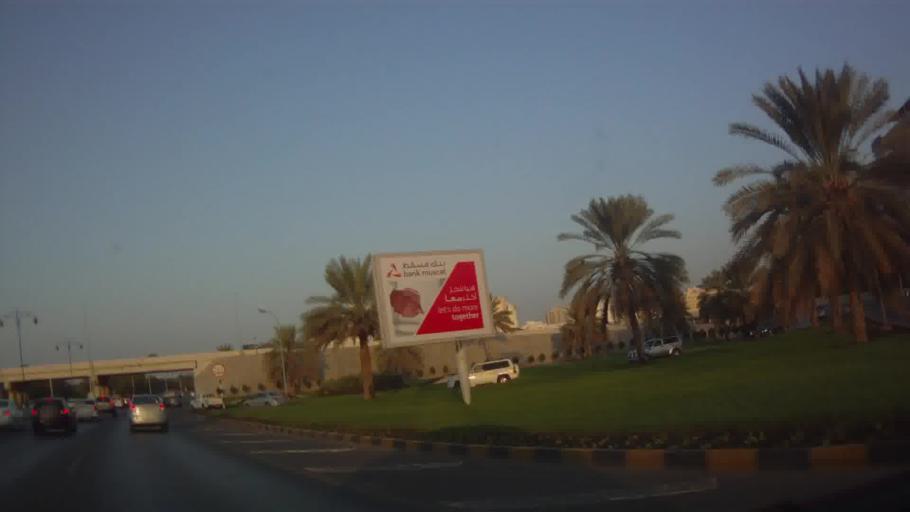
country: OM
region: Muhafazat Masqat
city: Bawshar
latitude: 23.5953
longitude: 58.4125
